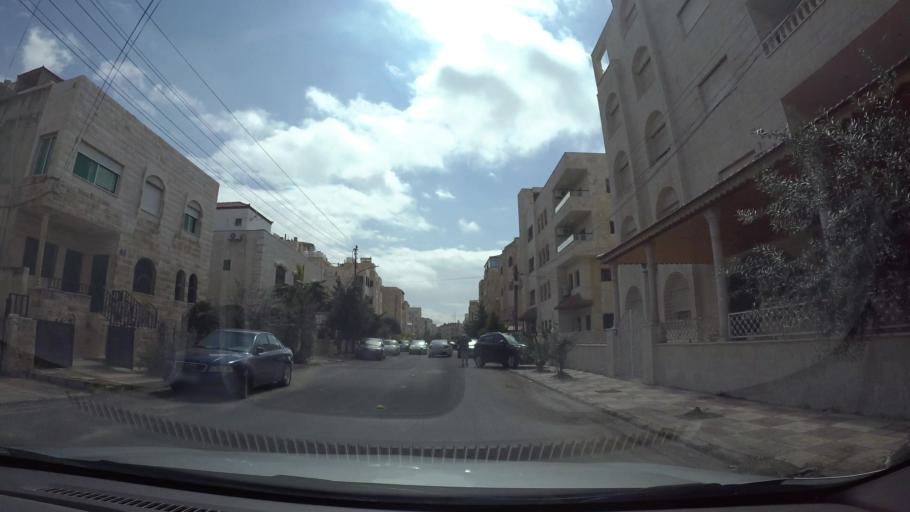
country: JO
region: Amman
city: Al Jubayhah
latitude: 31.9931
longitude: 35.8508
